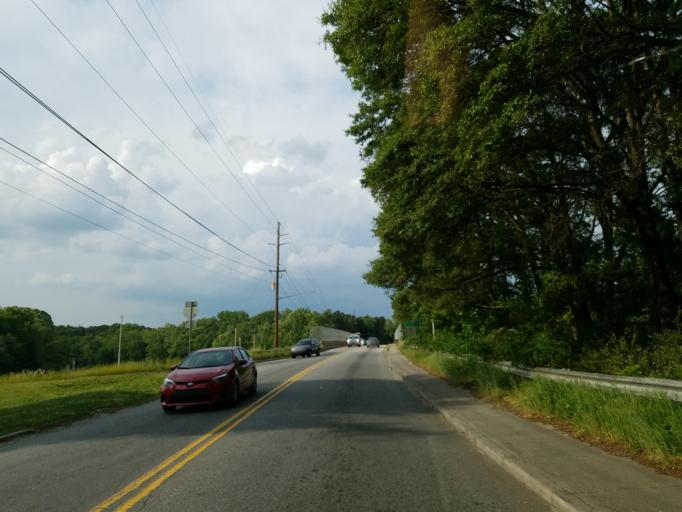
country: US
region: Georgia
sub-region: Cobb County
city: Vinings
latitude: 33.7983
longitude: -84.4888
